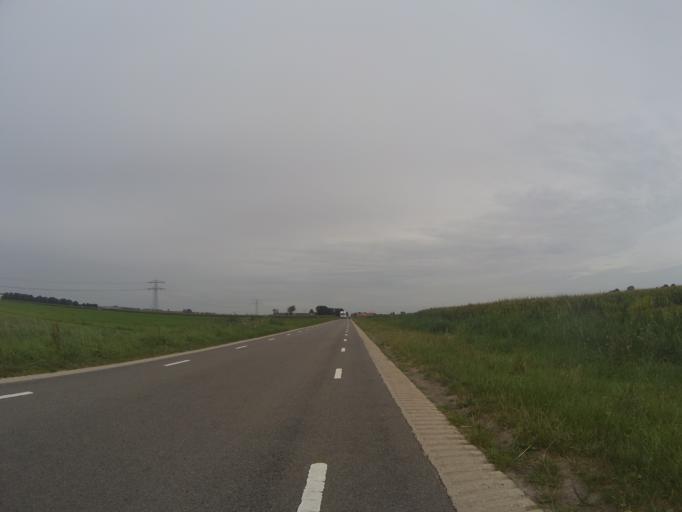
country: NL
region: Utrecht
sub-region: Gemeente Bunschoten
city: Bunschoten
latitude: 52.2223
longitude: 5.3904
